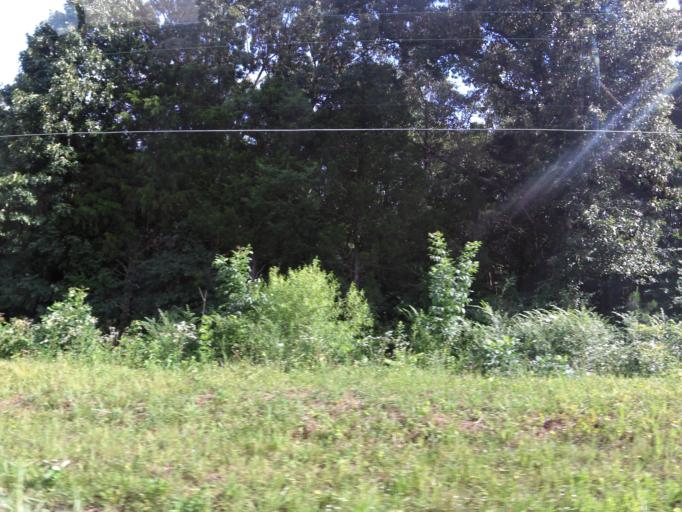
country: US
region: Tennessee
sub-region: Carroll County
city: Huntingdon
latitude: 36.0308
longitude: -88.3529
